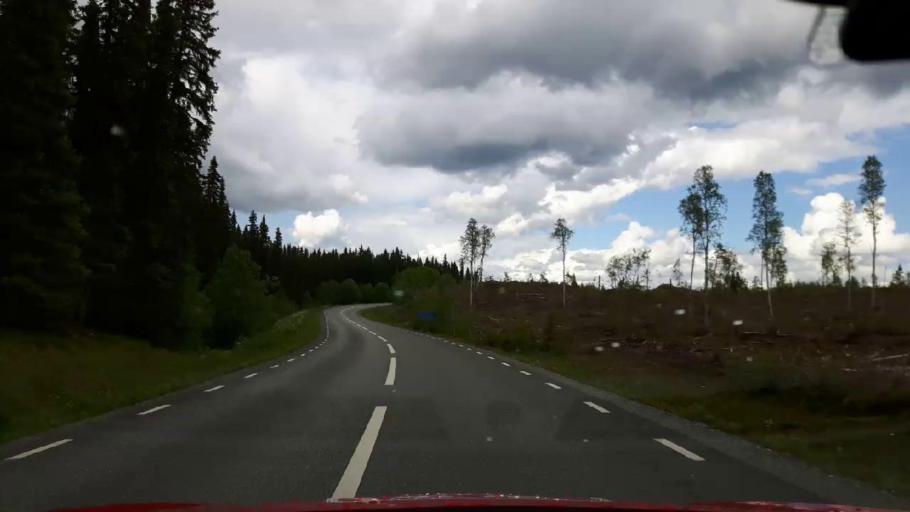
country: SE
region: Jaemtland
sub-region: Krokoms Kommun
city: Krokom
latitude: 63.7793
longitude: 14.3498
